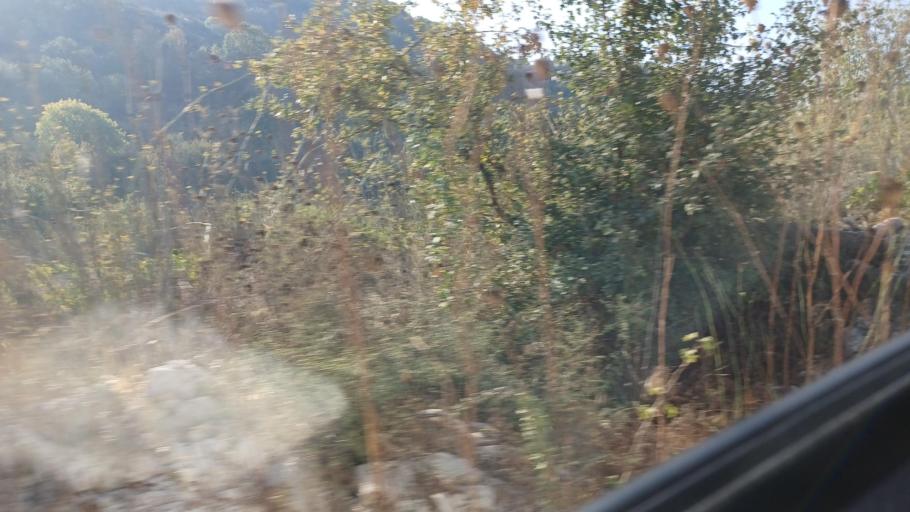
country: CY
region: Pafos
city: Mesogi
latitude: 34.8429
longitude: 32.4799
